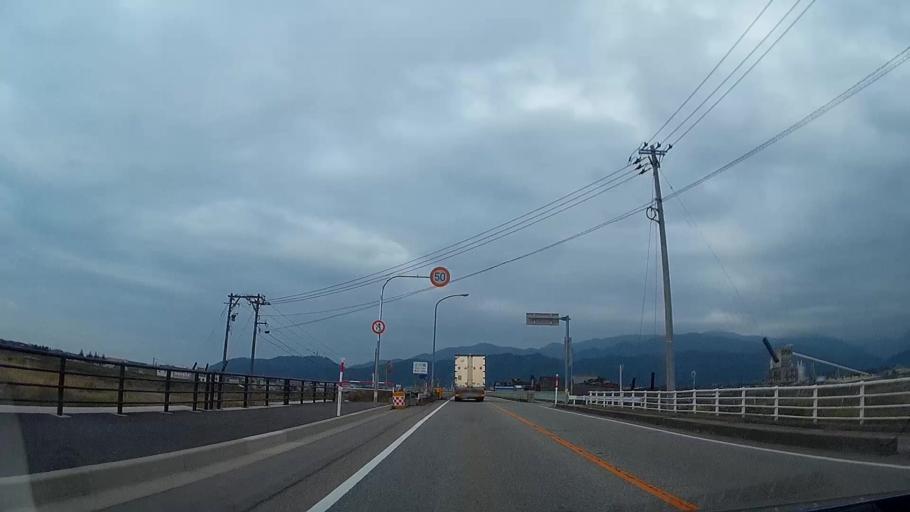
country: JP
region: Toyama
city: Nyuzen
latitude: 36.9459
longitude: 137.5393
